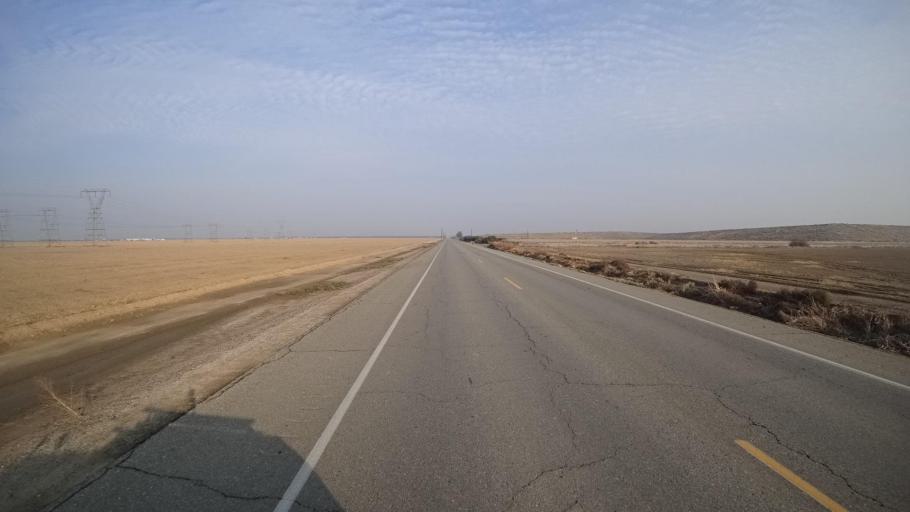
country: US
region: California
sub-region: Kern County
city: Weedpatch
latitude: 35.1854
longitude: -118.9146
